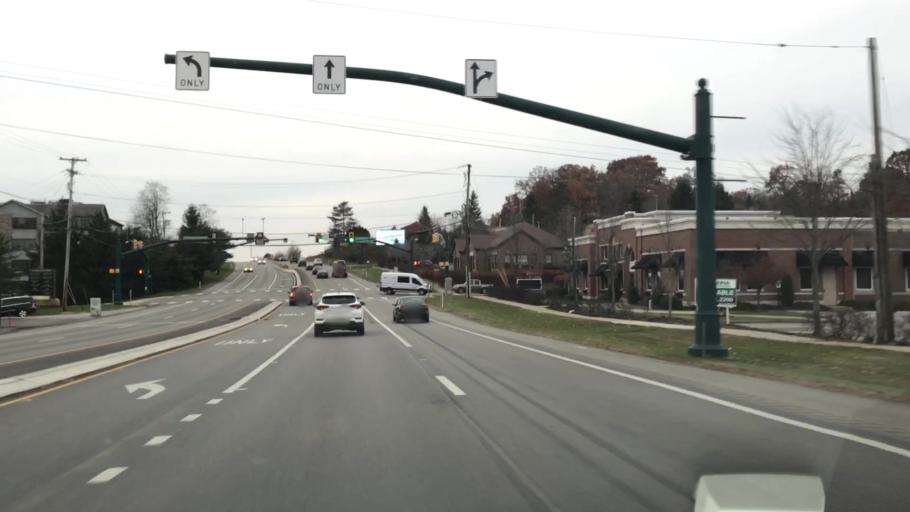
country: US
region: Pennsylvania
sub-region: Allegheny County
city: Bradford Woods
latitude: 40.6421
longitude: -80.0669
